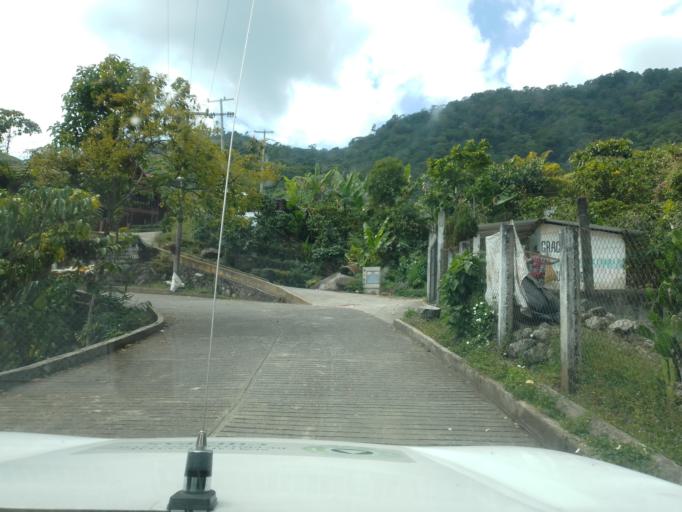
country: MX
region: Chiapas
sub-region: Union Juarez
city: Santo Domingo
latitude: 15.0606
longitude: -92.0941
